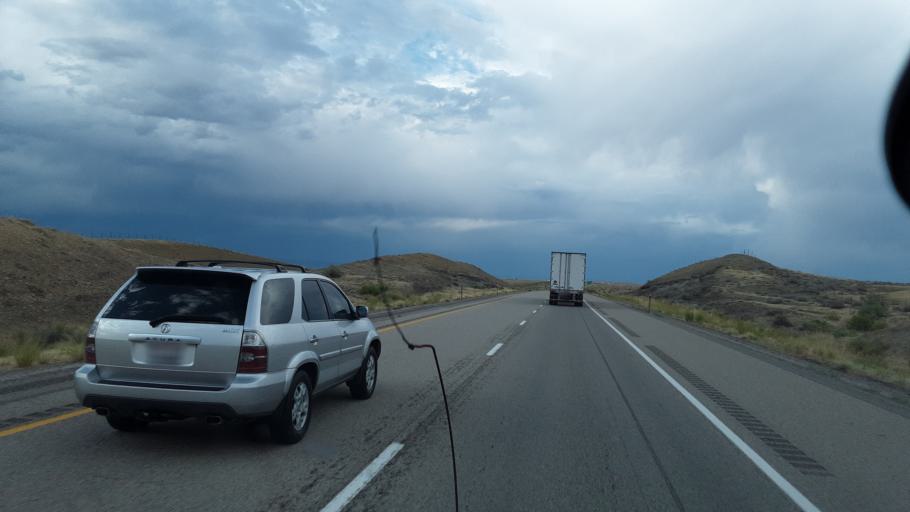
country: US
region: Colorado
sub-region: Mesa County
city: Loma
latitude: 39.0285
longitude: -109.2912
